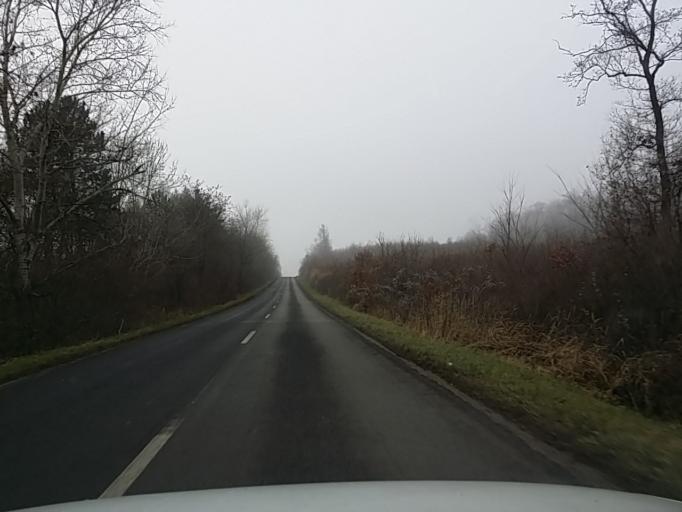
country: HU
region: Pest
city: Budakeszi
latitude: 47.5254
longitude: 18.8875
